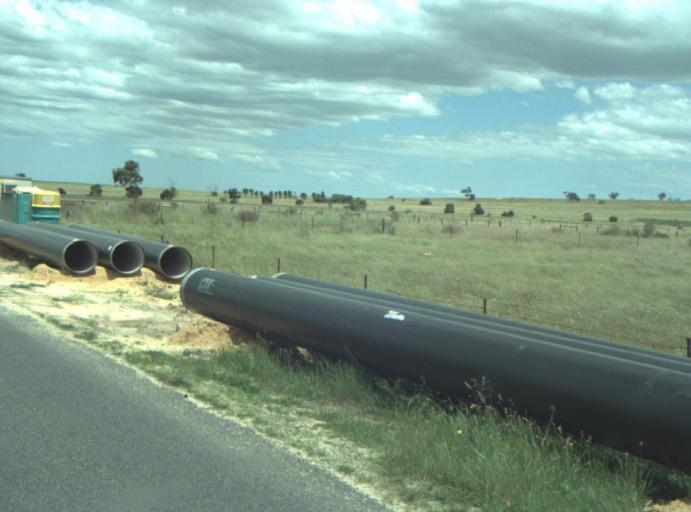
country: AU
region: Victoria
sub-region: Wyndham
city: Little River
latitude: -37.9322
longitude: 144.4652
